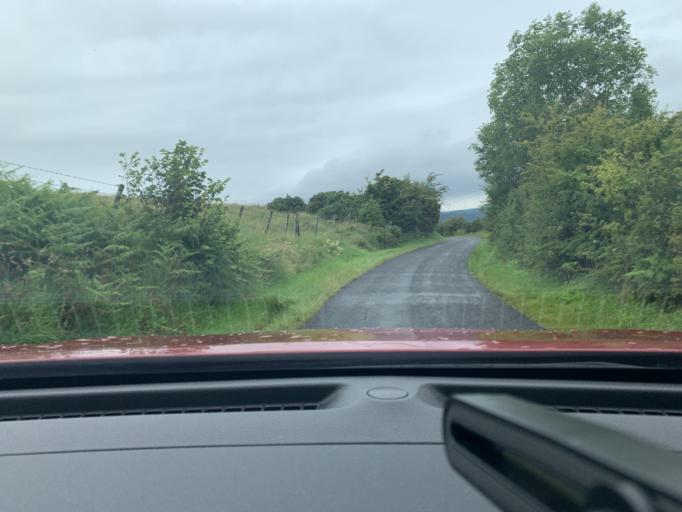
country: GB
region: Northern Ireland
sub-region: Fermanagh District
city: Enniskillen
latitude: 54.2739
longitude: -7.8565
